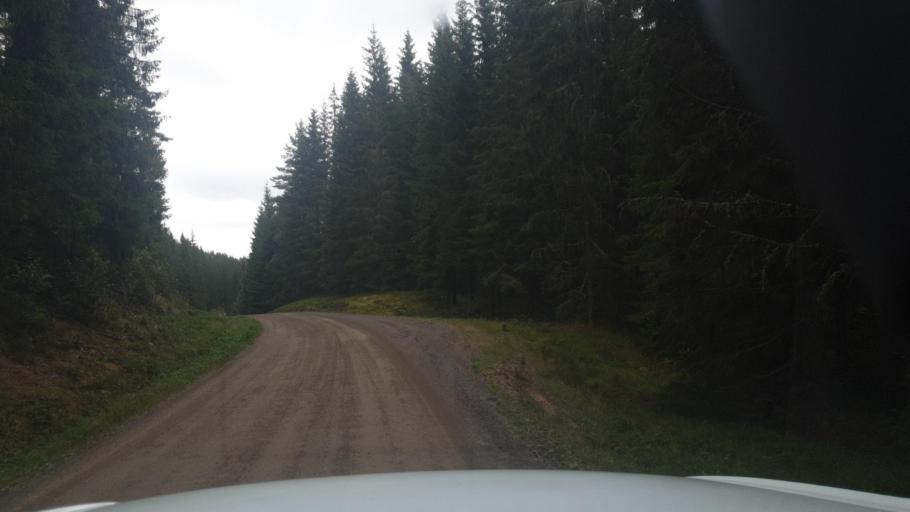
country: SE
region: Vaermland
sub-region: Sunne Kommun
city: Sunne
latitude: 59.8618
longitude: 12.8739
